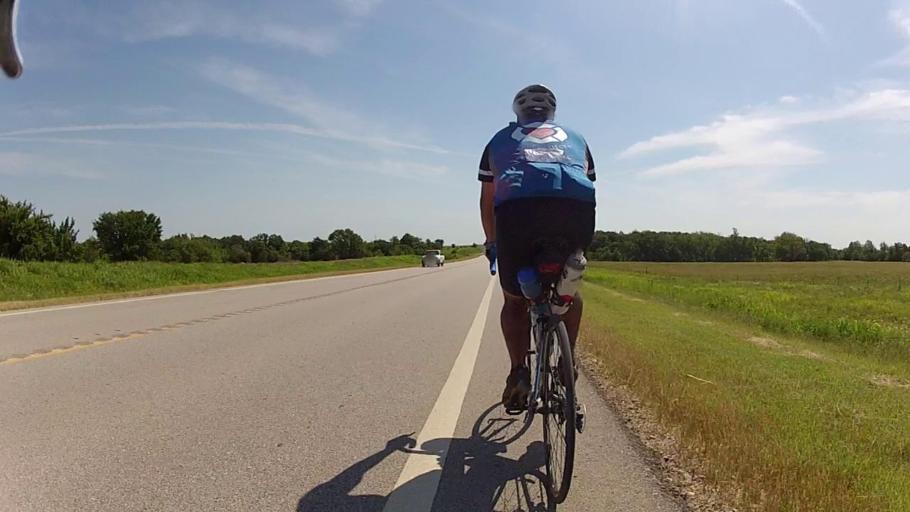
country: US
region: Kansas
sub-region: Chautauqua County
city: Sedan
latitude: 37.1086
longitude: -96.5340
